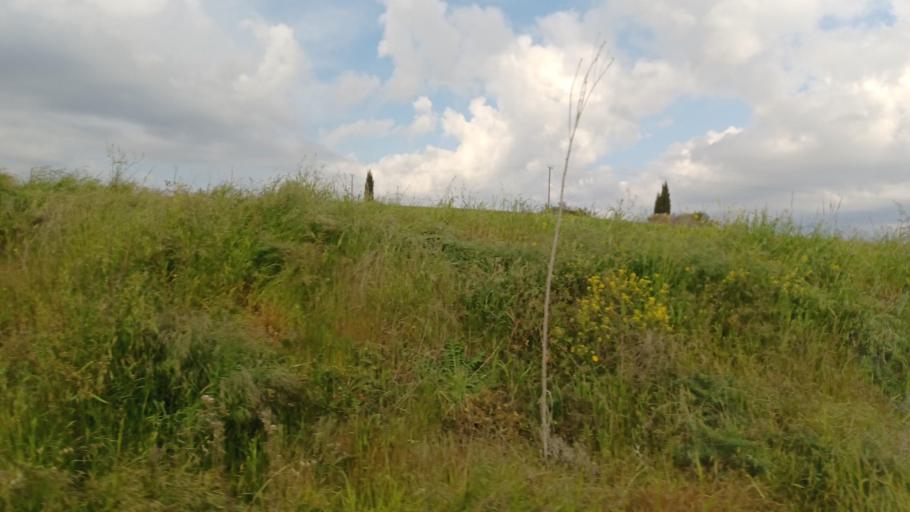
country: CY
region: Lefkosia
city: Kakopetria
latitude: 35.0727
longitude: 32.9435
